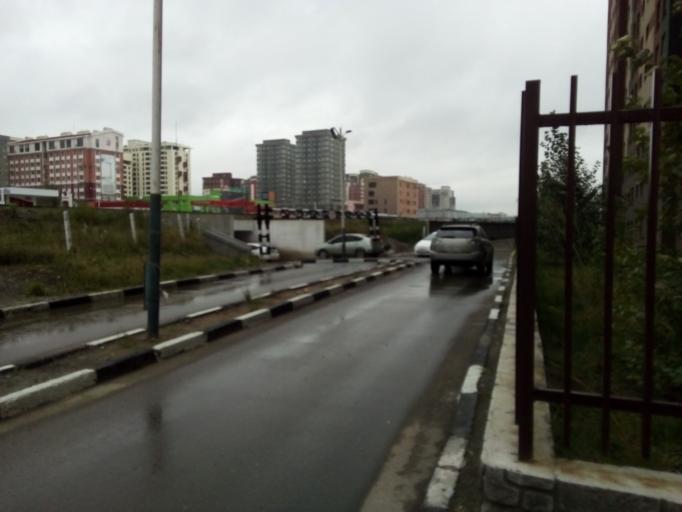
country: MN
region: Ulaanbaatar
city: Ulaanbaatar
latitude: 47.9072
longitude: 106.9356
